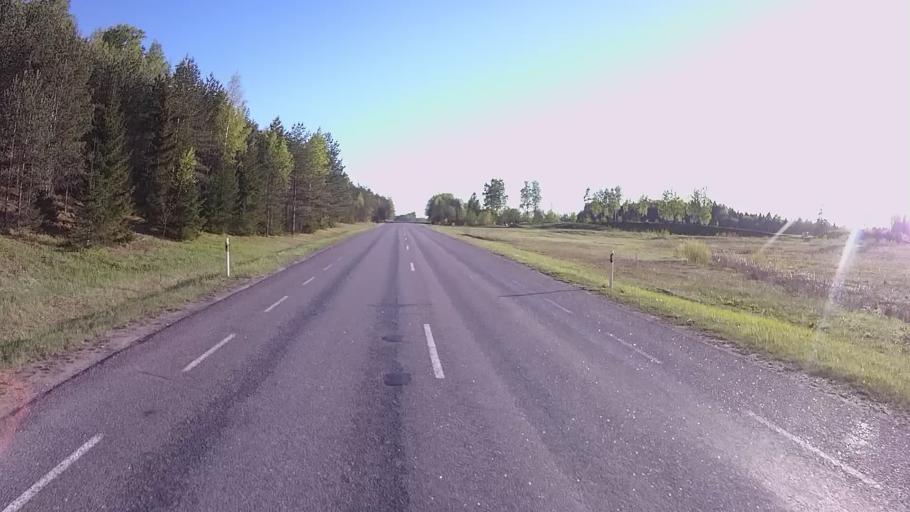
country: EE
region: Viljandimaa
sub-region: Viiratsi vald
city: Viiratsi
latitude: 58.4151
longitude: 25.6883
